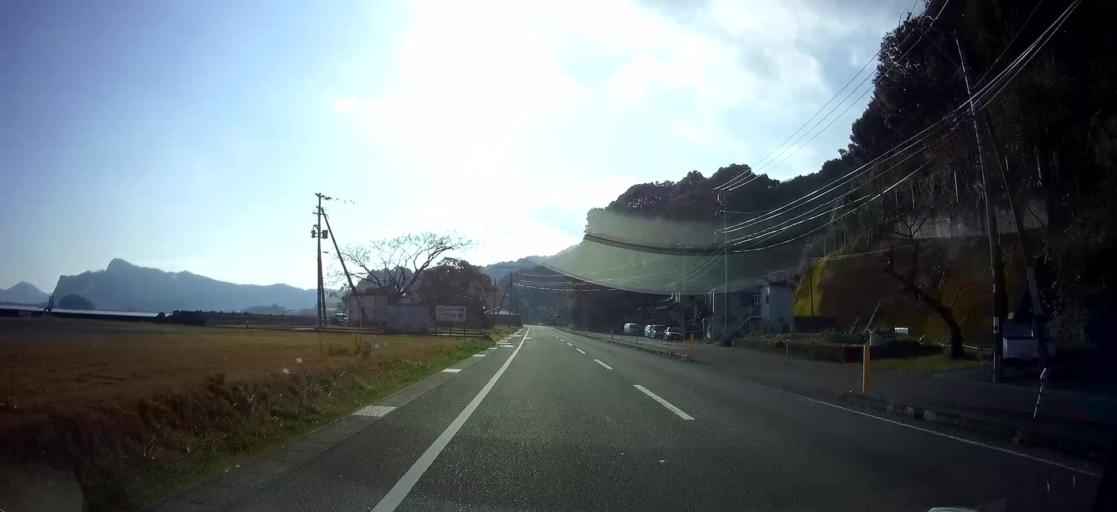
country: JP
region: Kumamoto
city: Yatsushiro
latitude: 32.4507
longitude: 130.4189
